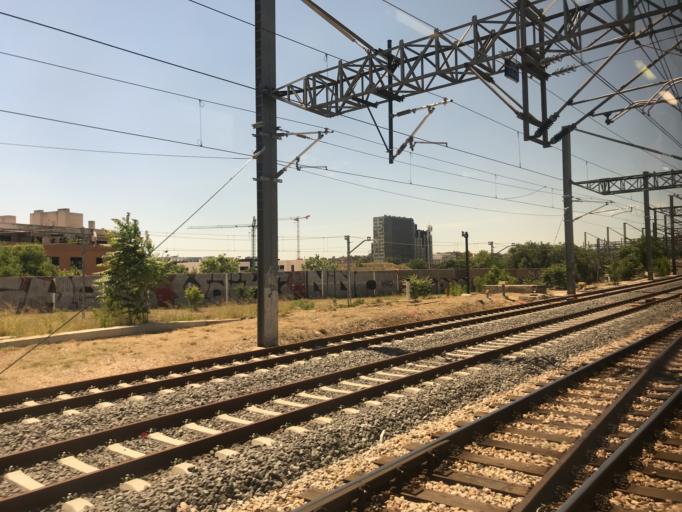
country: ES
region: Madrid
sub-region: Provincia de Madrid
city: Retiro
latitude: 40.3990
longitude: -3.6768
